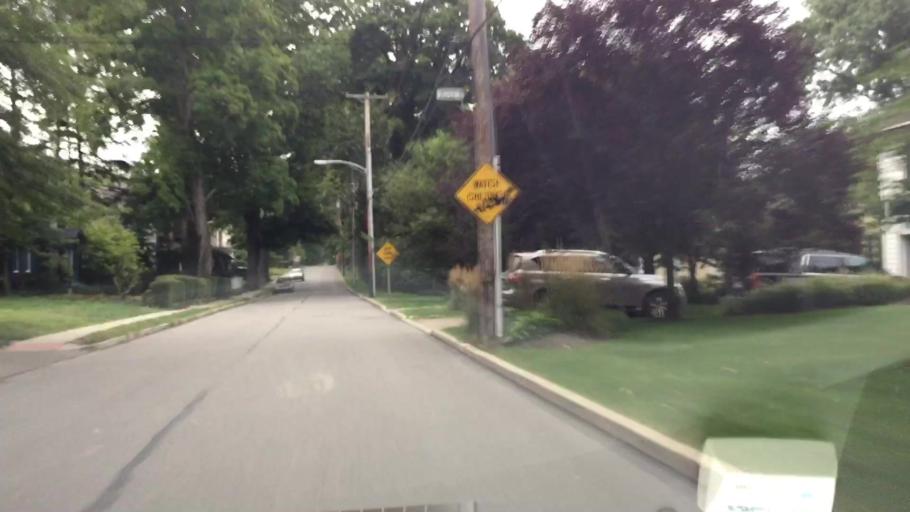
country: US
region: Pennsylvania
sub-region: Allegheny County
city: Edgeworth
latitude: 40.5532
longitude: -80.1893
